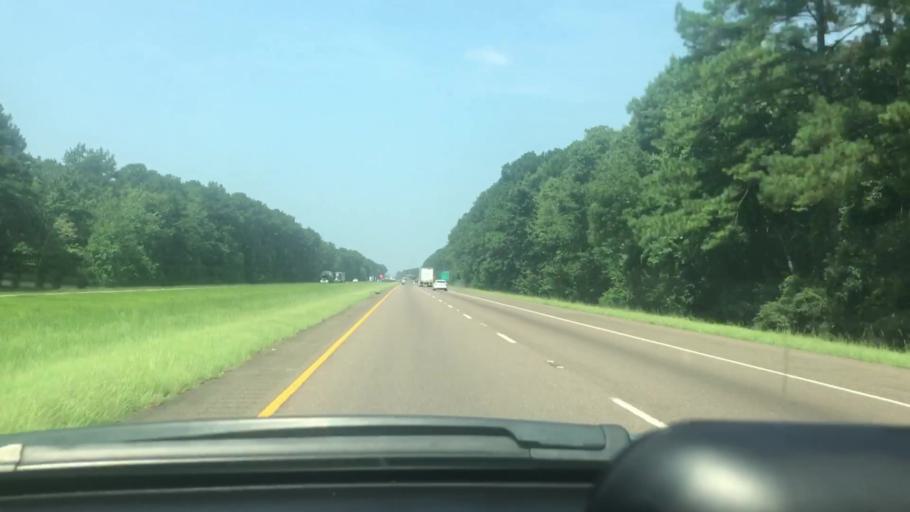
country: US
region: Louisiana
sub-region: Livingston Parish
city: Livingston
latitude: 30.4741
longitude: -90.7728
